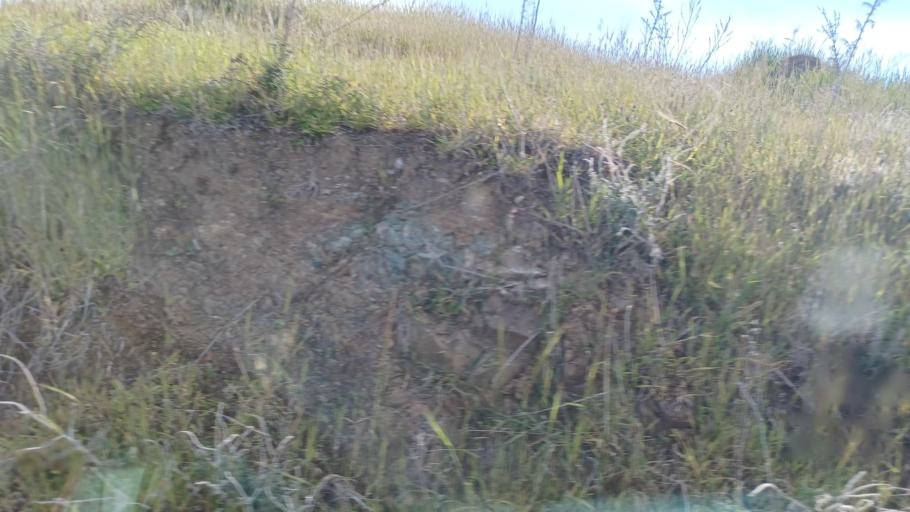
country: CY
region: Lefkosia
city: Kakopetria
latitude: 35.0785
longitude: 32.9534
